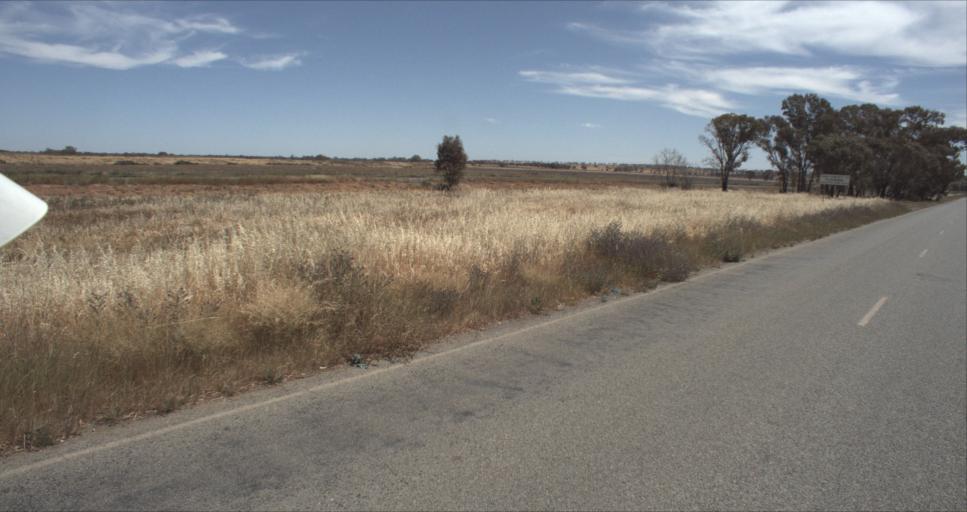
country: AU
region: New South Wales
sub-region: Leeton
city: Leeton
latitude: -34.6431
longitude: 146.4687
